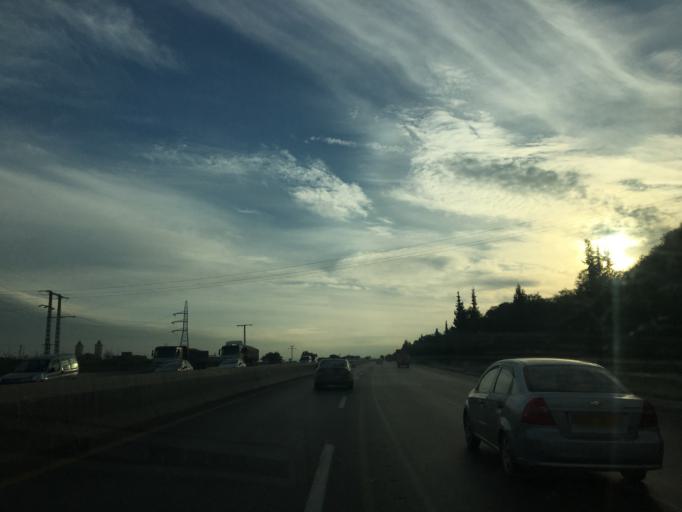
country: DZ
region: Bouira
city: Draa el Mizan
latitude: 36.4751
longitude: 3.7517
